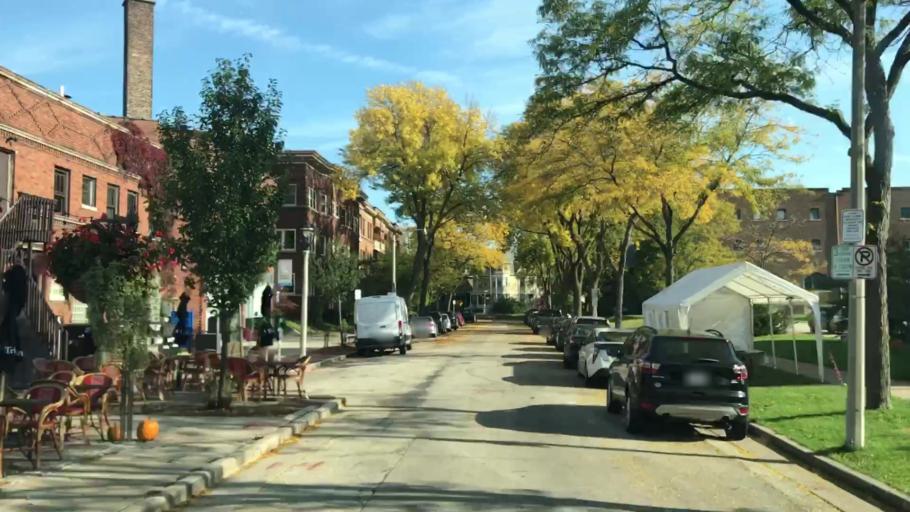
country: US
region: Wisconsin
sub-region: Milwaukee County
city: Shorewood
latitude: 43.0662
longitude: -87.8778
